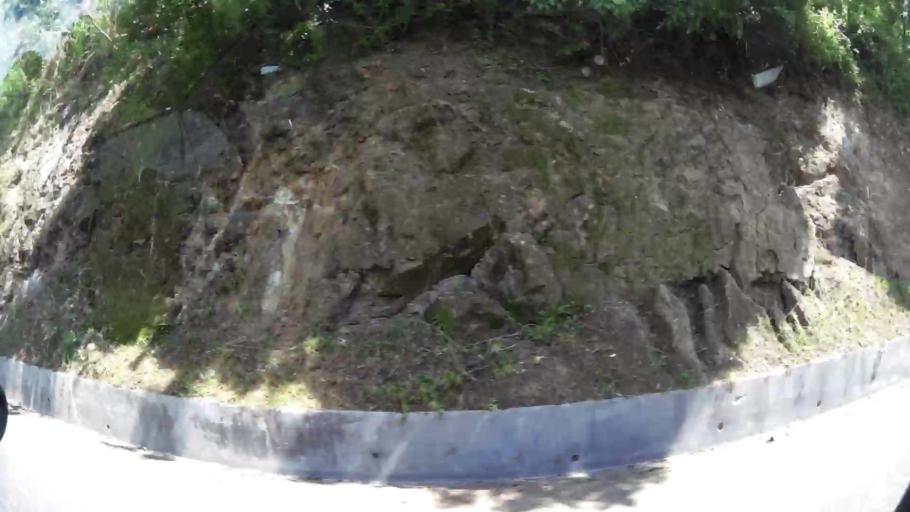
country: TT
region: Tobago
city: Scarborough
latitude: 11.2351
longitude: -60.7376
